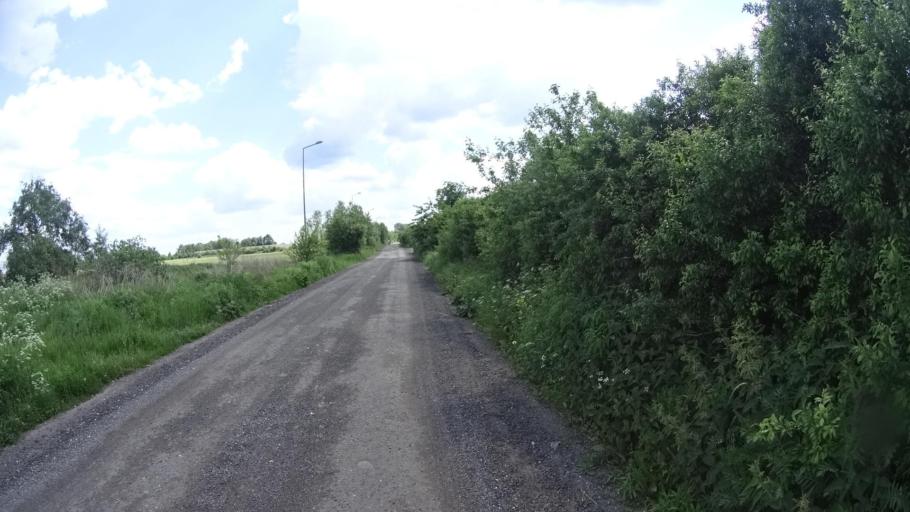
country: PL
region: Masovian Voivodeship
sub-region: Powiat pruszkowski
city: Nadarzyn
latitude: 52.0577
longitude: 20.8235
